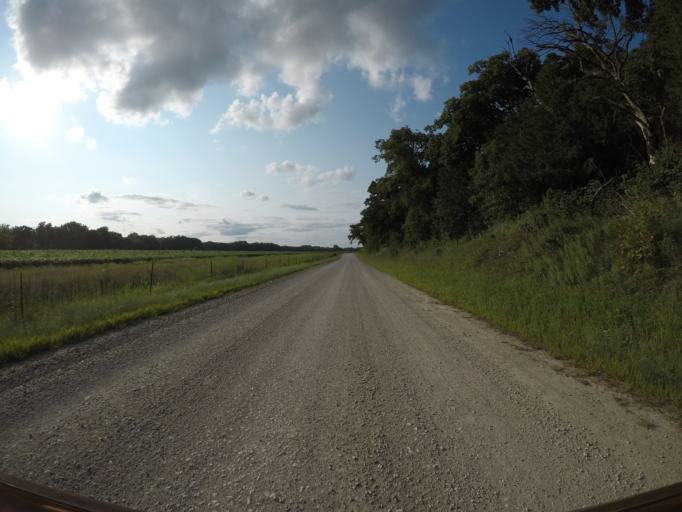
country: US
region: Kansas
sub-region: Wabaunsee County
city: Alma
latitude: 38.9006
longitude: -96.2080
